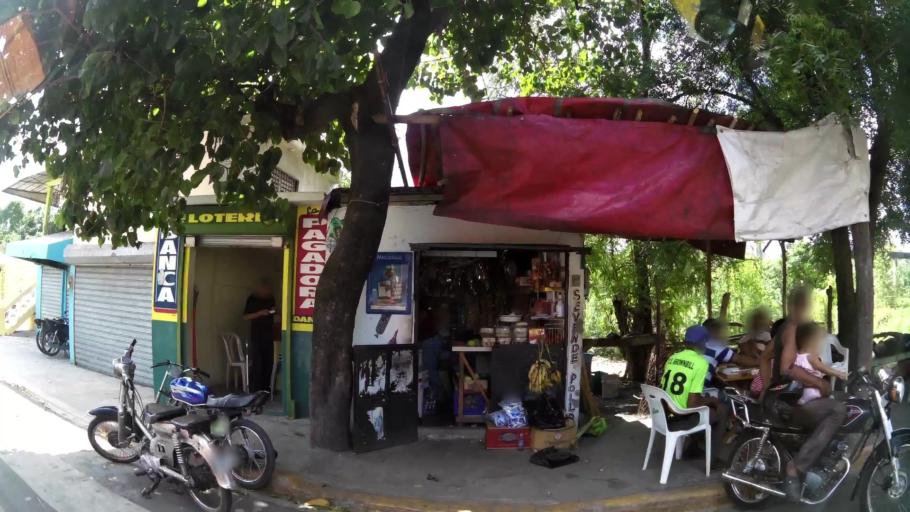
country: DO
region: San Cristobal
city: San Cristobal
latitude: 18.4209
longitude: -70.0946
